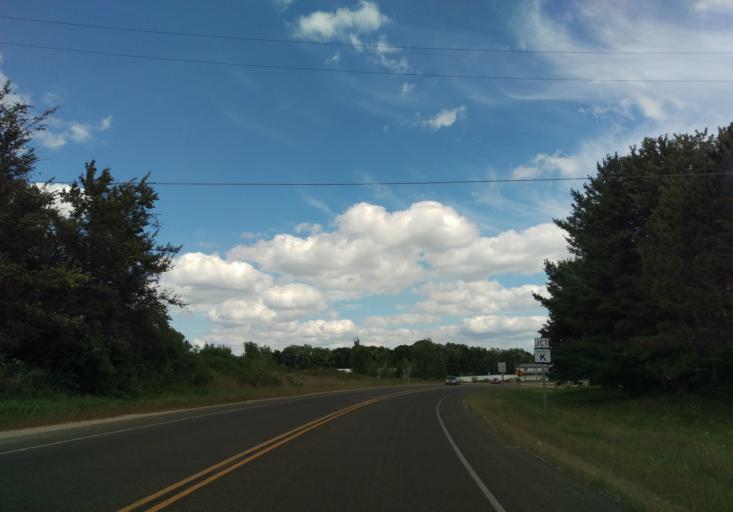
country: US
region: Wisconsin
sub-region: Dane County
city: Waunakee
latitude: 43.1445
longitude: -89.4418
